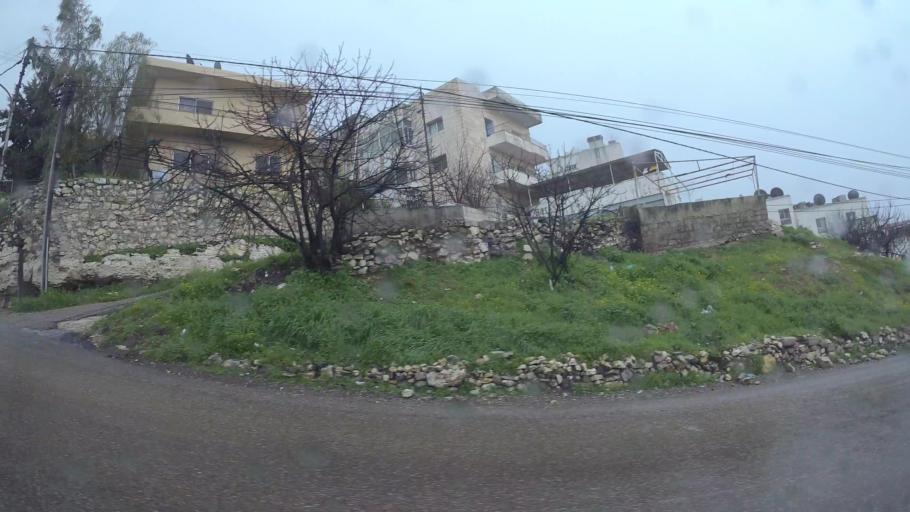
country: JO
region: Amman
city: Wadi as Sir
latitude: 32.0023
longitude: 35.7876
